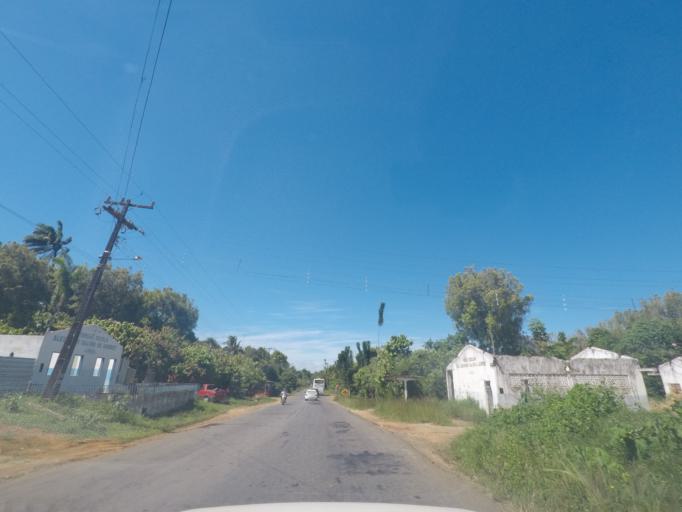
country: BR
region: Bahia
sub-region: Valenca
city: Valenca
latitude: -13.4313
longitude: -39.0777
